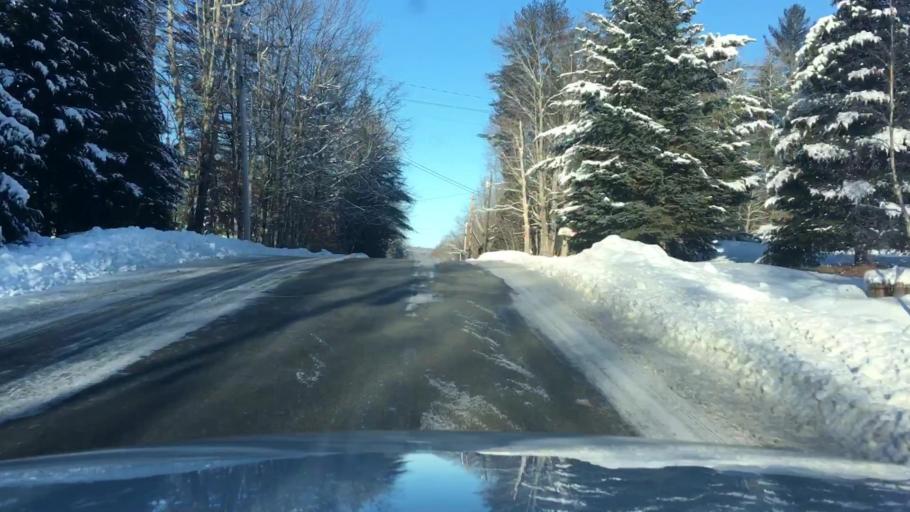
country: US
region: Maine
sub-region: Kennebec County
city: Belgrade
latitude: 44.4235
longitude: -69.8875
